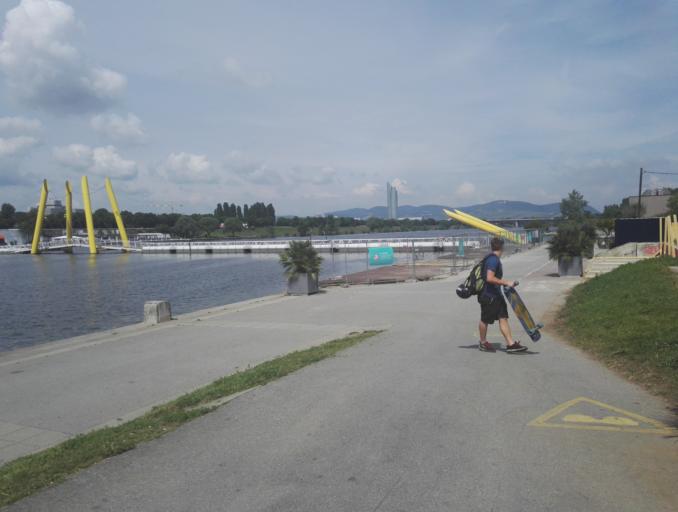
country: AT
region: Vienna
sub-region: Wien Stadt
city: Vienna
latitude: 48.2307
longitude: 16.4111
